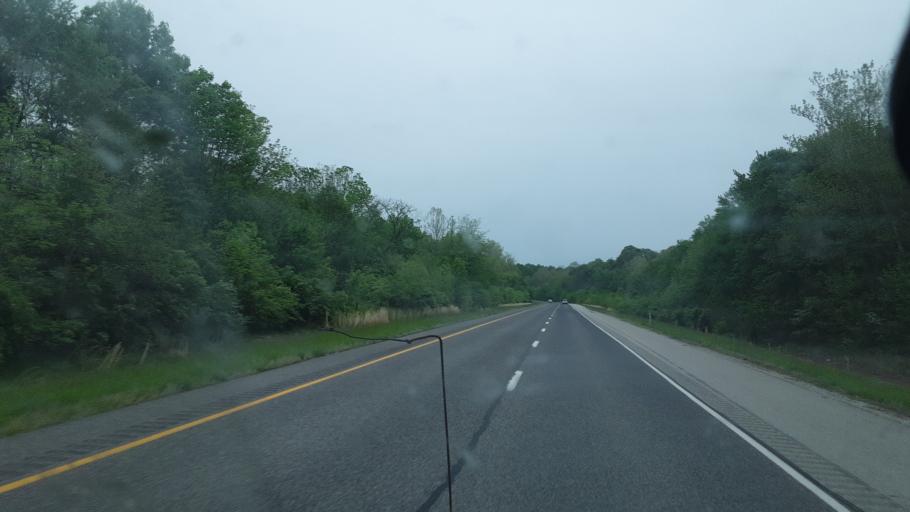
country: US
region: Indiana
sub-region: Warrick County
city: Boonville
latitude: 38.2009
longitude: -87.2340
